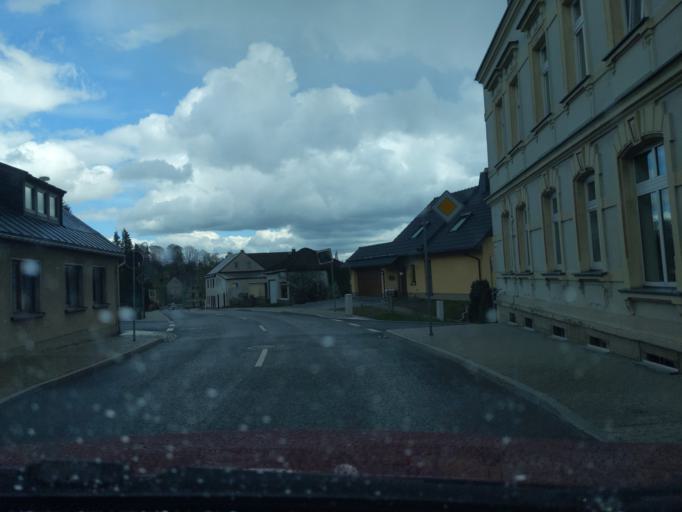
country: DE
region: Saxony
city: Schoenheide
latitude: 50.5037
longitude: 12.5070
